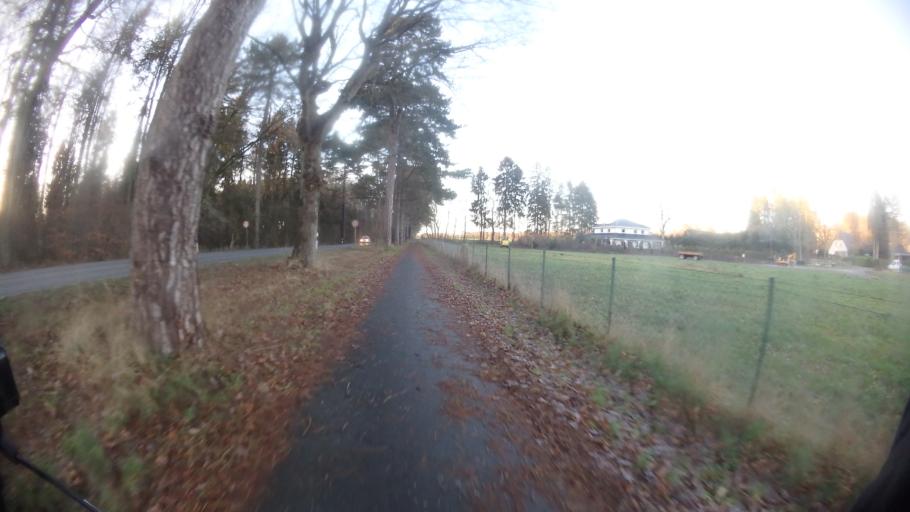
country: DE
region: Schleswig-Holstein
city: Scharbeutz
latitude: 54.0055
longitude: 10.6963
